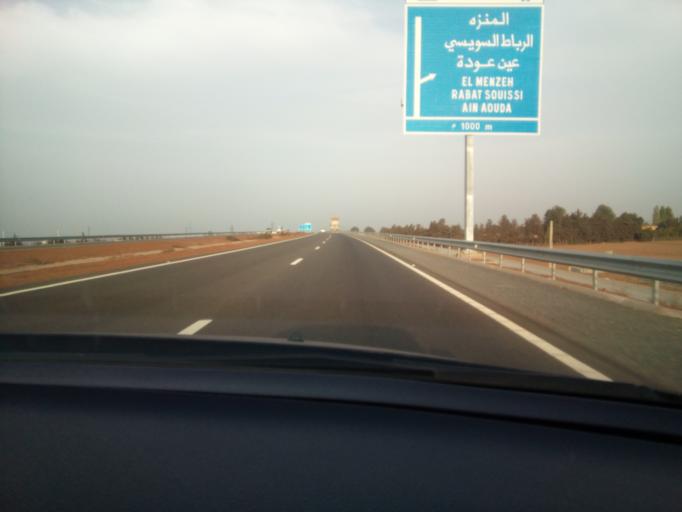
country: MA
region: Rabat-Sale-Zemmour-Zaer
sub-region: Skhirate-Temara
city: Temara
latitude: 33.8416
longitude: -6.8520
